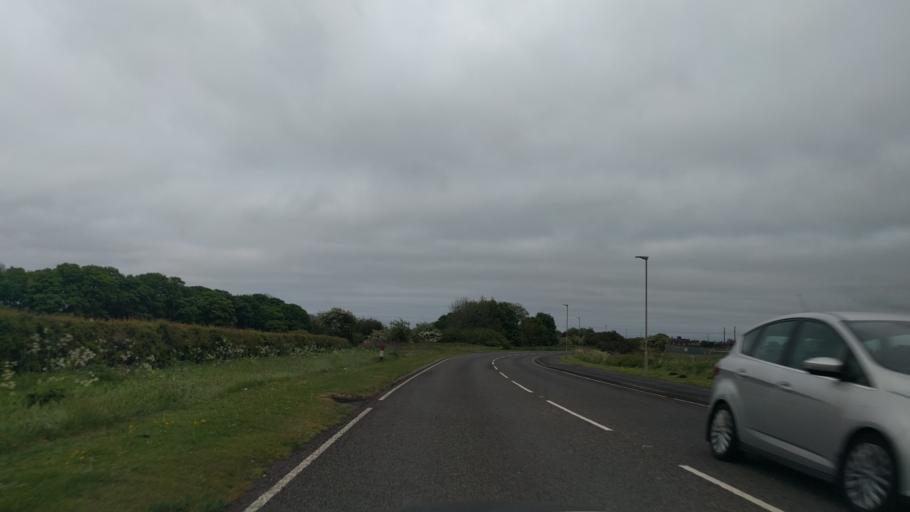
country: GB
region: England
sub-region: Northumberland
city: Choppington
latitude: 55.1605
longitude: -1.6188
